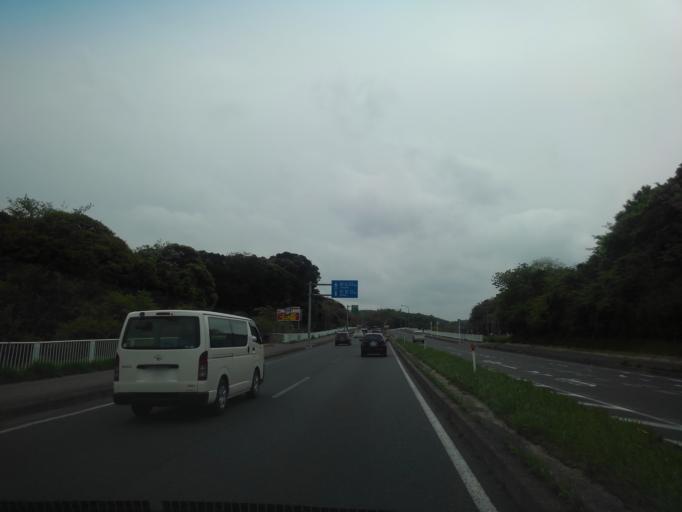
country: JP
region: Chiba
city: Kisarazu
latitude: 35.3564
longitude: 139.9207
